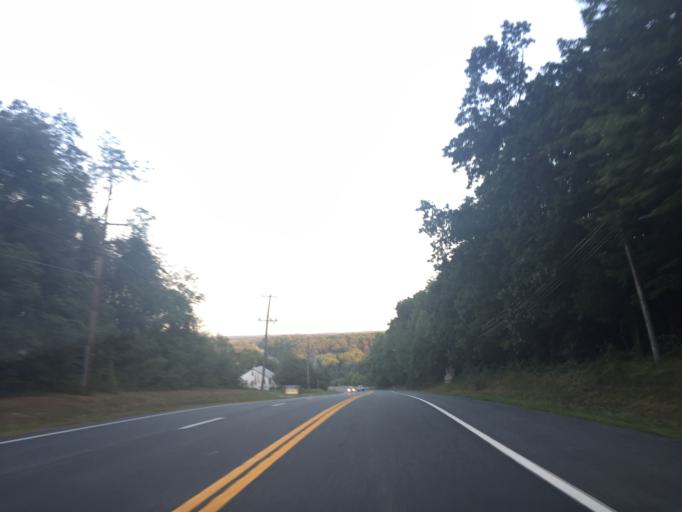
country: US
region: Pennsylvania
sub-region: York County
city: Susquehanna Trails
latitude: 39.7034
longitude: -76.3367
